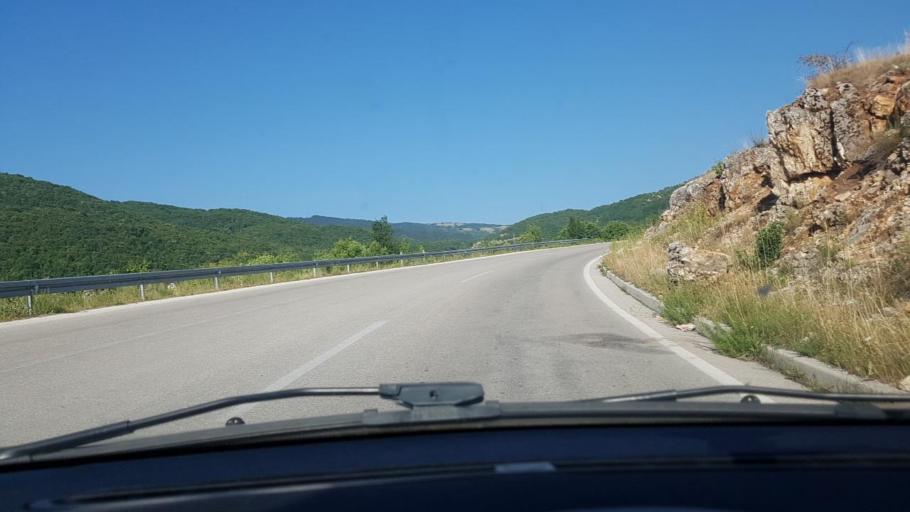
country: BA
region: Federation of Bosnia and Herzegovina
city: Rumboci
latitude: 43.8186
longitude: 17.4651
